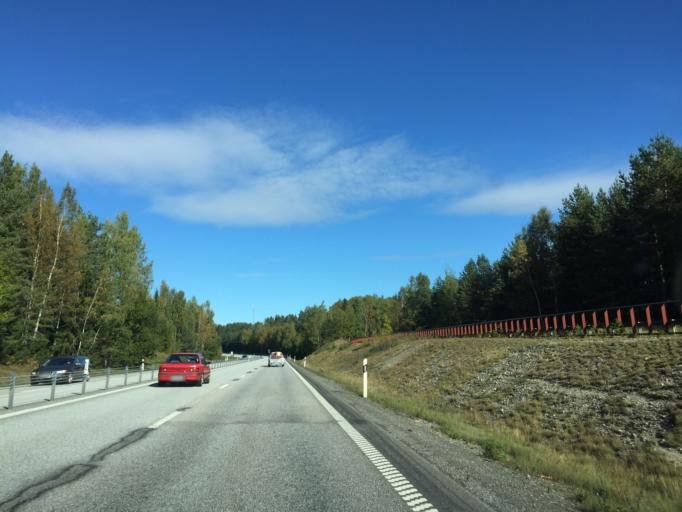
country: SE
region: OErebro
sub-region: Orebro Kommun
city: Hovsta
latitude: 59.3380
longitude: 15.2368
